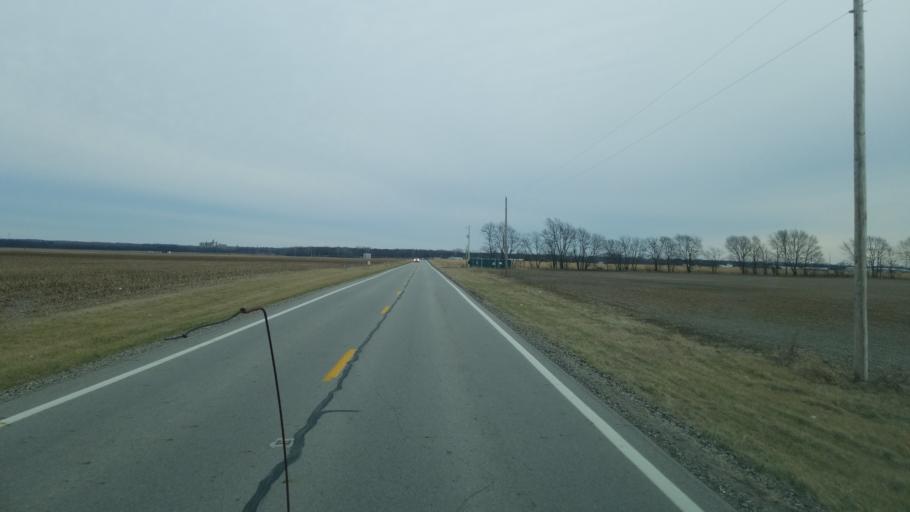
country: US
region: Ohio
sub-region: Pickaway County
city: Circleville
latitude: 39.6056
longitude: -82.9912
